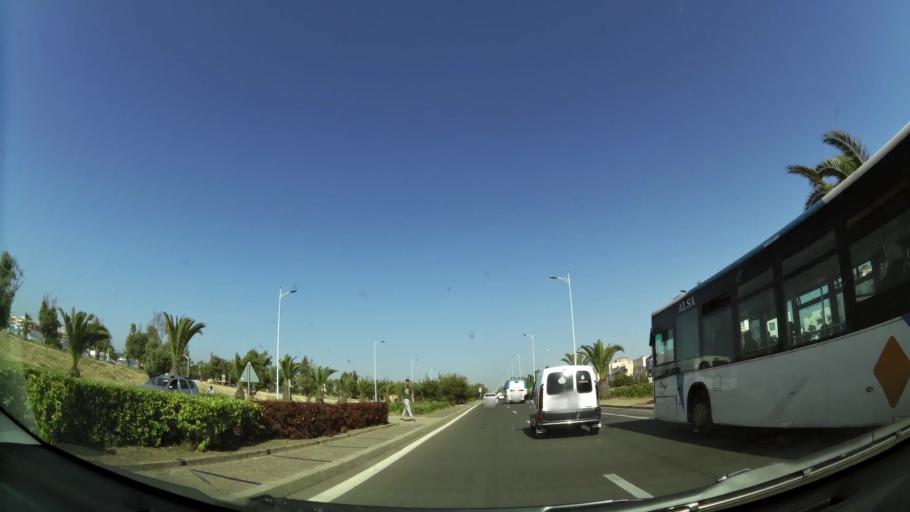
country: MA
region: Oued ed Dahab-Lagouira
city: Dakhla
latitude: 30.4041
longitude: -9.5488
